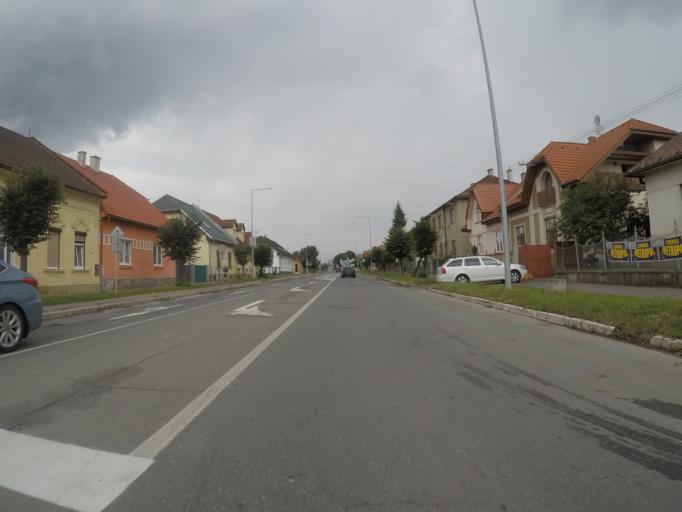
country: SK
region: Kosicky
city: Spisska Nova Ves
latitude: 48.9475
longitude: 20.5572
